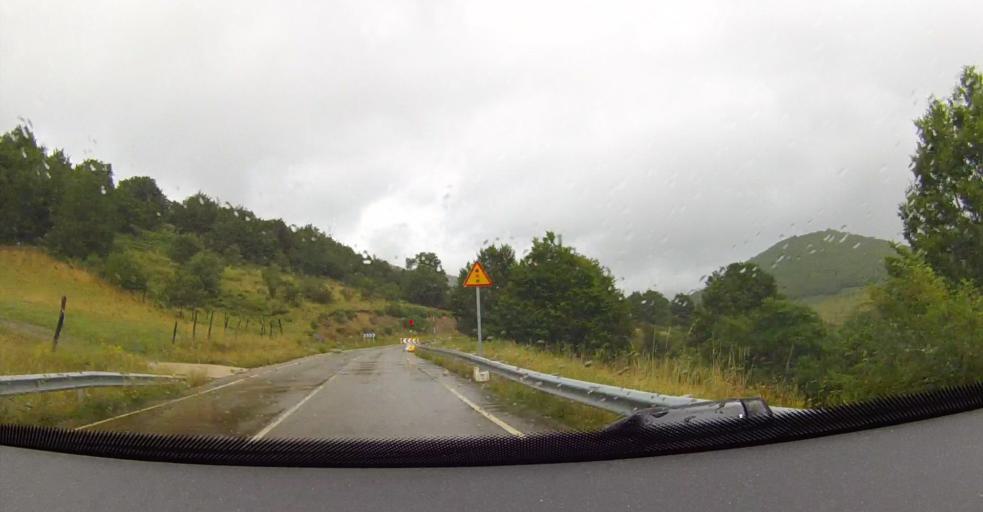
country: ES
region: Castille and Leon
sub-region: Provincia de Leon
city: Marana
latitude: 43.0715
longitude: -5.1673
